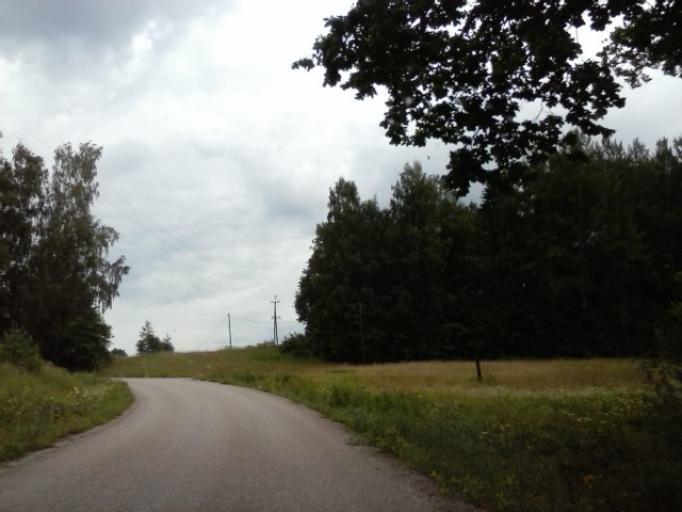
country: EE
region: Vorumaa
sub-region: Voru linn
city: Voru
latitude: 57.7406
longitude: 27.1052
